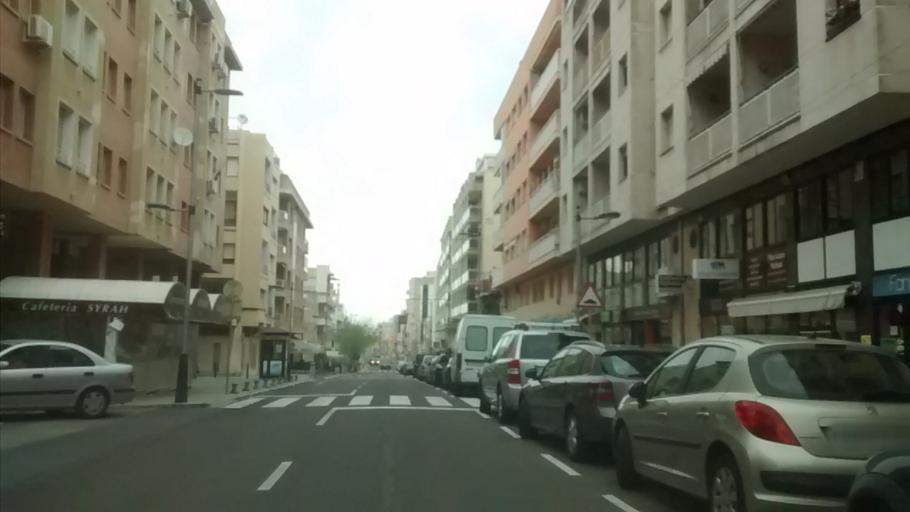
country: ES
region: Catalonia
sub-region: Provincia de Tarragona
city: Sant Carles de la Rapita
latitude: 40.6161
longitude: 0.5885
